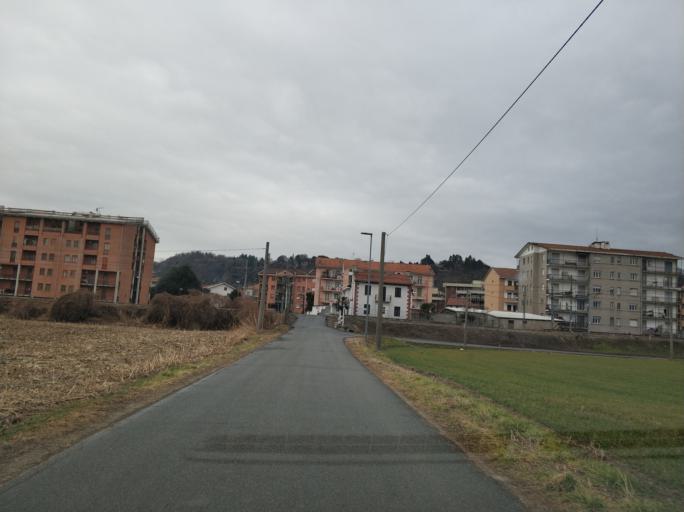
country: IT
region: Piedmont
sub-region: Provincia di Torino
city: Ivrea
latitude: 45.4552
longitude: 7.8819
